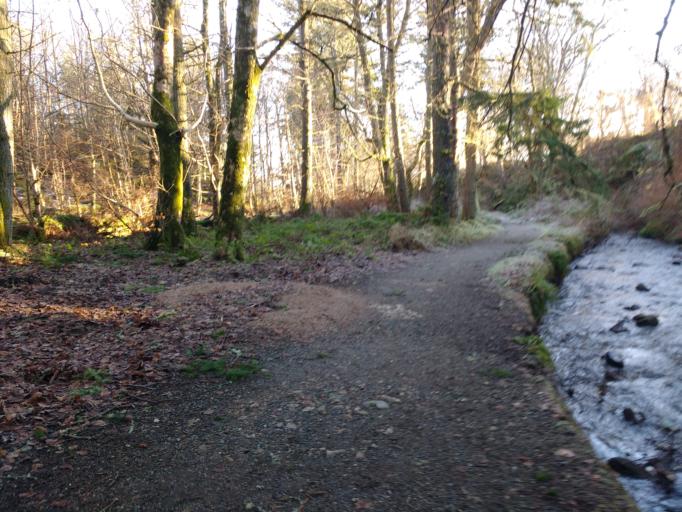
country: GB
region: Scotland
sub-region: Eilean Siar
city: Isle of Lewis
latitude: 58.2191
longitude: -6.3947
